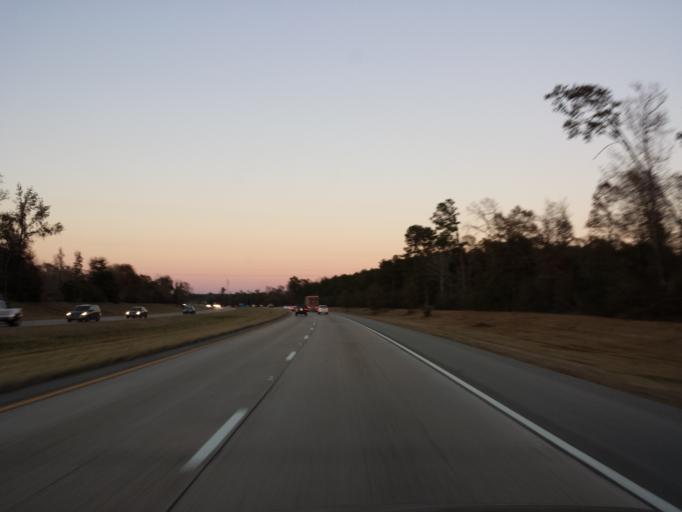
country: US
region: Mississippi
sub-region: Jones County
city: Ellisville
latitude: 31.5094
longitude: -89.2948
